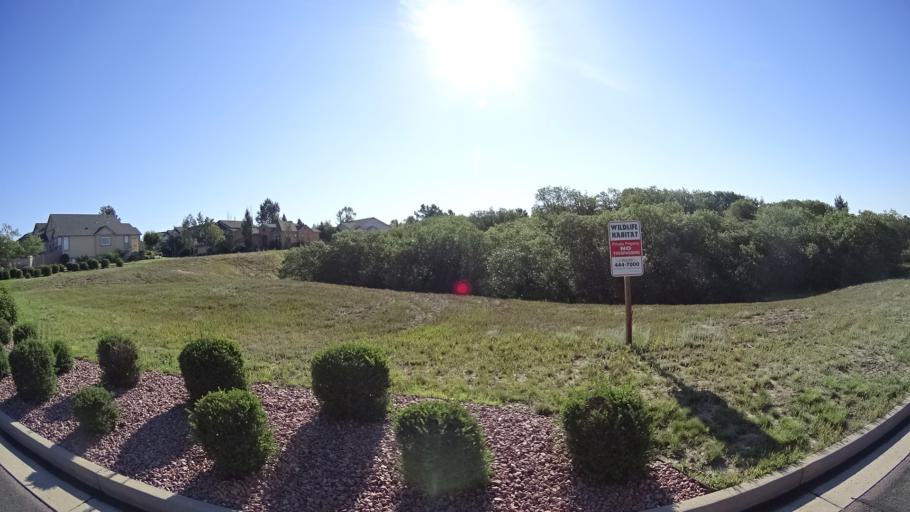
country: US
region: Colorado
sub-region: El Paso County
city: Black Forest
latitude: 38.9748
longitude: -104.7580
